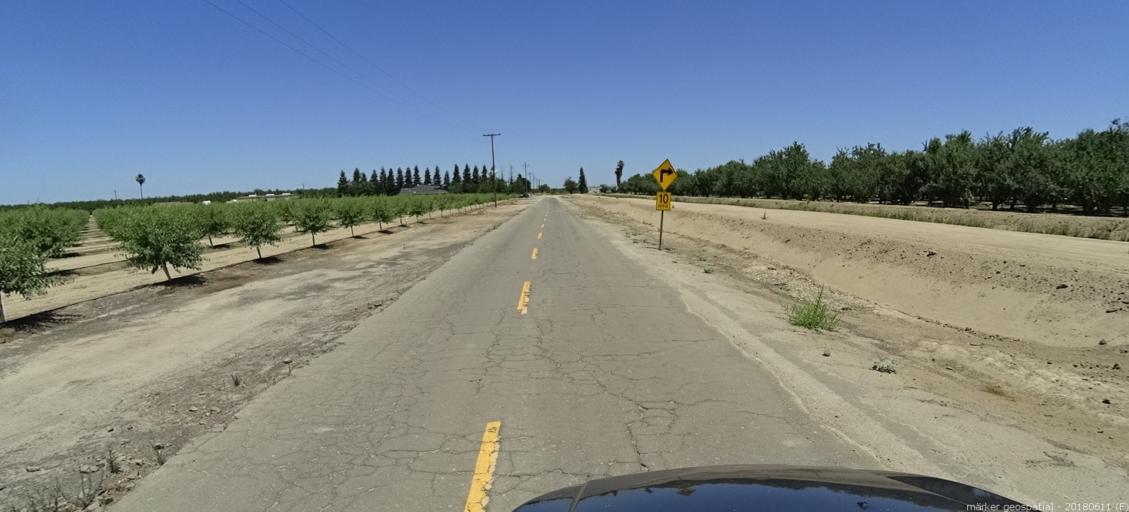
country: US
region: California
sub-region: Madera County
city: Fairmead
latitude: 37.0524
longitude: -120.2205
